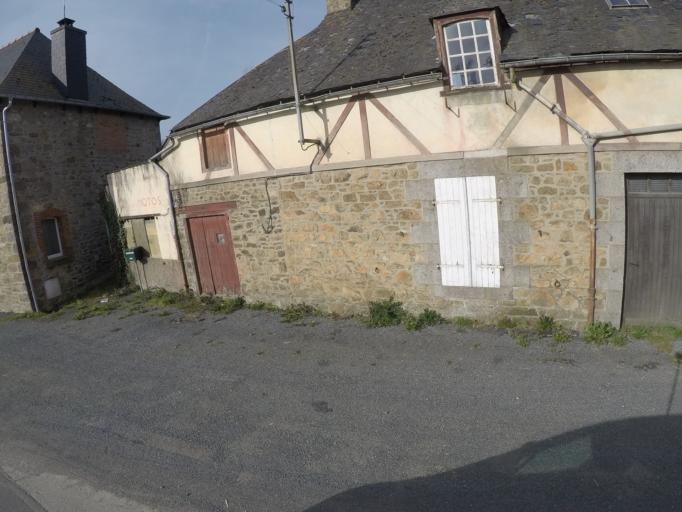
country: FR
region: Brittany
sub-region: Departement des Cotes-d'Armor
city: Plouagat
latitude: 48.5328
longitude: -2.9728
